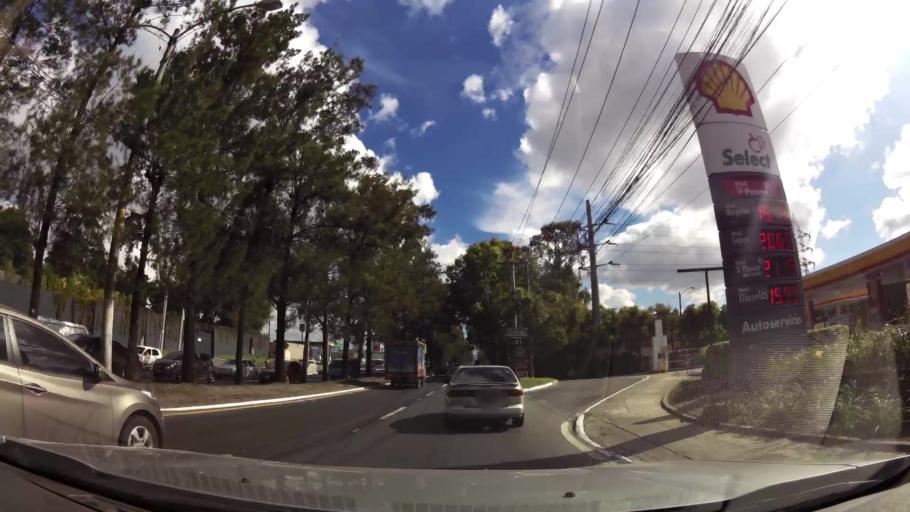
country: GT
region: Guatemala
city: Guatemala City
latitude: 14.6224
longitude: -90.5581
